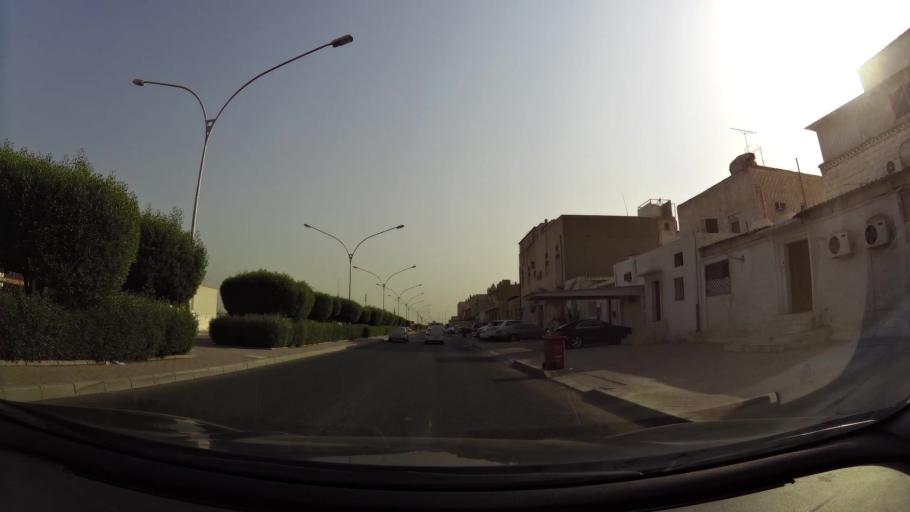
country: KW
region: Al Ahmadi
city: Ar Riqqah
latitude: 29.1151
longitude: 48.1053
